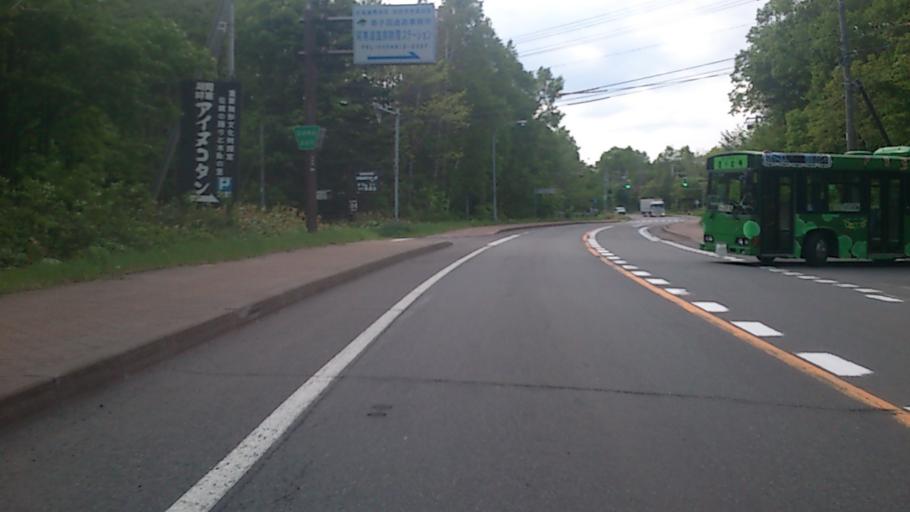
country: JP
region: Hokkaido
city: Bihoro
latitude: 43.4324
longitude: 144.0895
